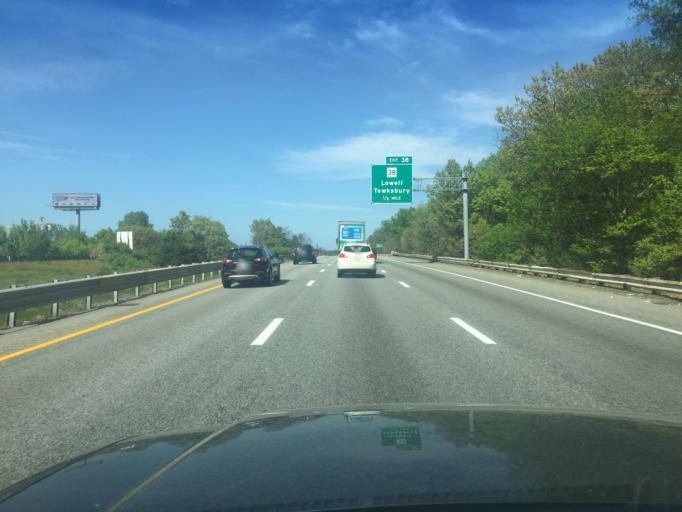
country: US
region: Massachusetts
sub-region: Middlesex County
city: Lowell
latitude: 42.6235
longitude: -71.2786
